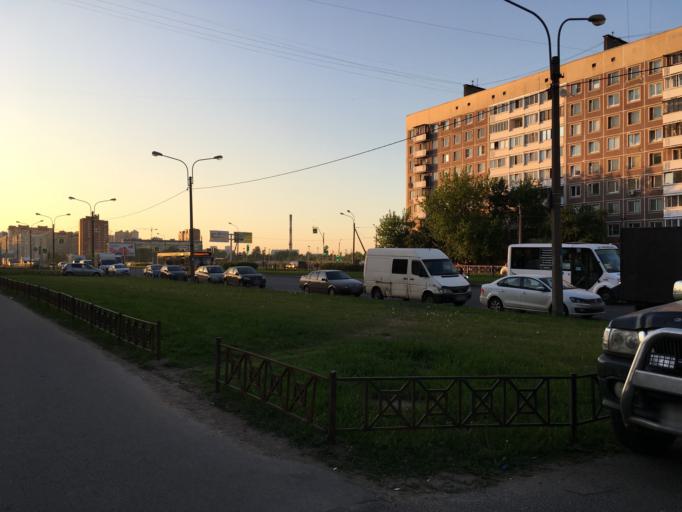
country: RU
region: St.-Petersburg
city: Komendantsky aerodrom
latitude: 60.0141
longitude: 30.2617
